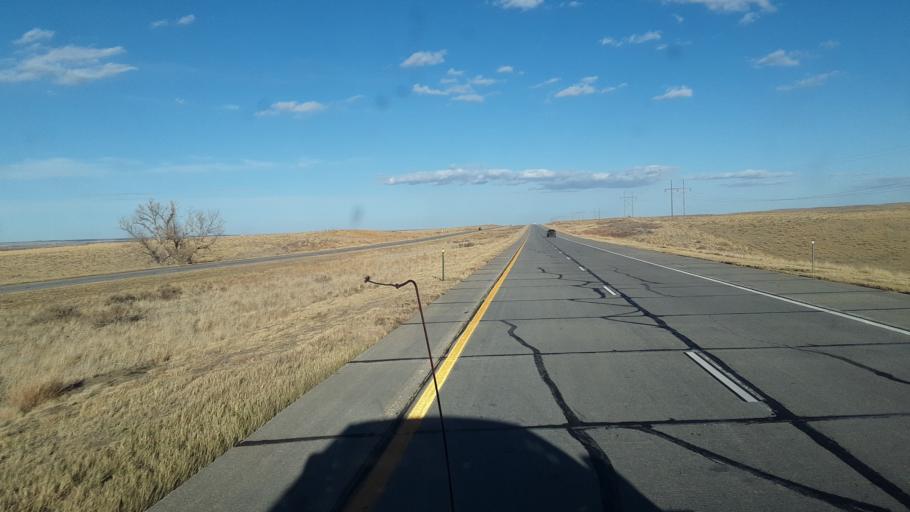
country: US
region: Nebraska
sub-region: Cheyenne County
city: Sidney
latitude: 40.8042
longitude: -102.8585
